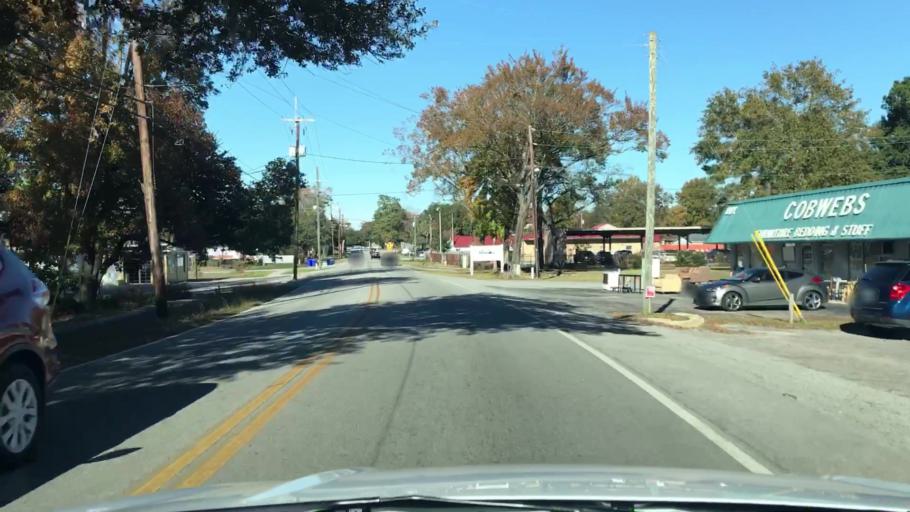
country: US
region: South Carolina
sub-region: Charleston County
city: North Charleston
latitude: 32.7960
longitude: -80.0163
